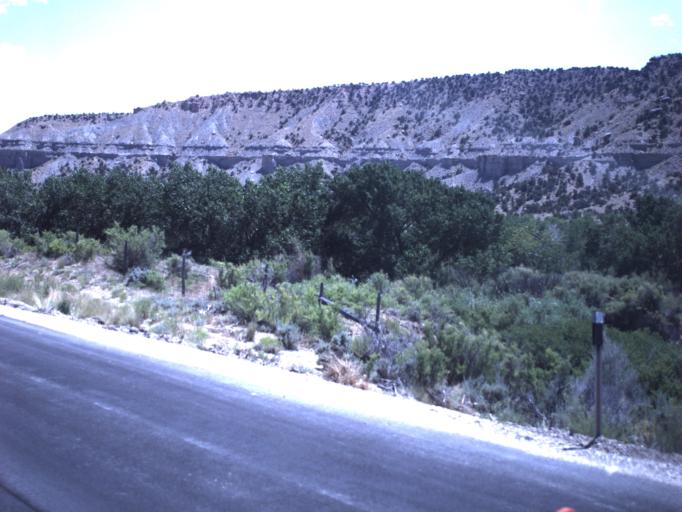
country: US
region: Utah
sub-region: Emery County
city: Orangeville
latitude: 39.2634
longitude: -111.1230
